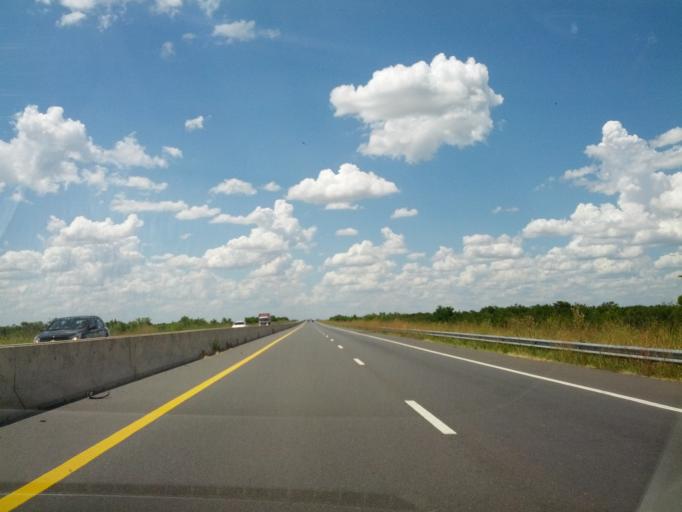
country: AR
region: Entre Rios
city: Colonia Elia
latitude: -32.7746
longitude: -58.5040
